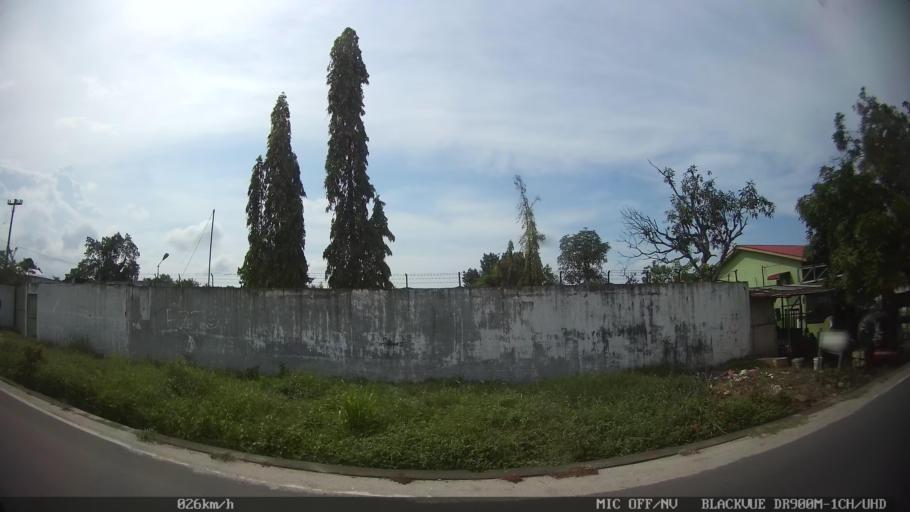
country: ID
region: North Sumatra
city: Percut
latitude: 3.6094
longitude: 98.7970
